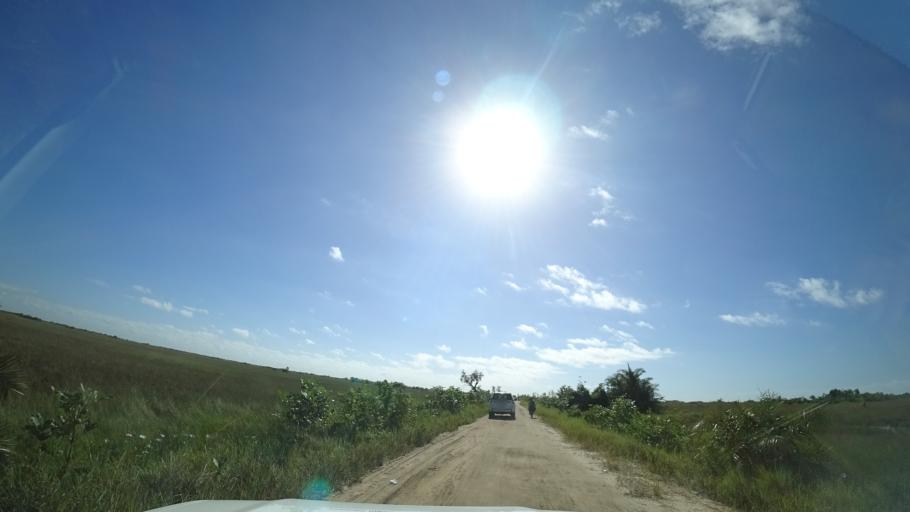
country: MZ
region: Sofala
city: Beira
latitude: -19.6979
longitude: 35.0306
